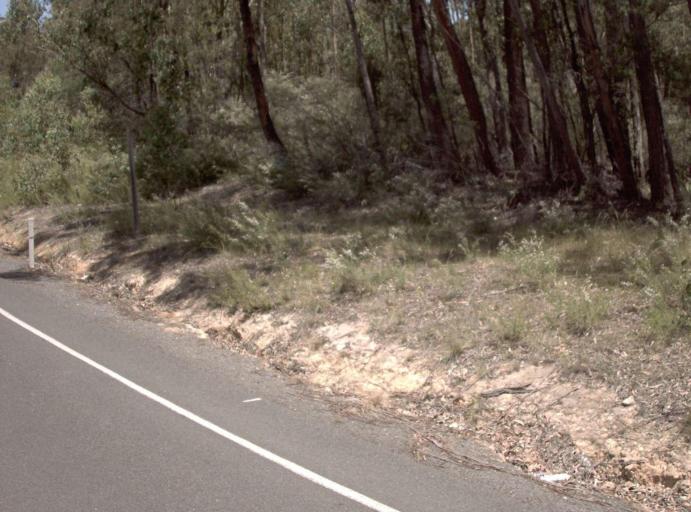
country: AU
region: Victoria
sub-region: East Gippsland
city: Lakes Entrance
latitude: -37.5933
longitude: 147.8931
